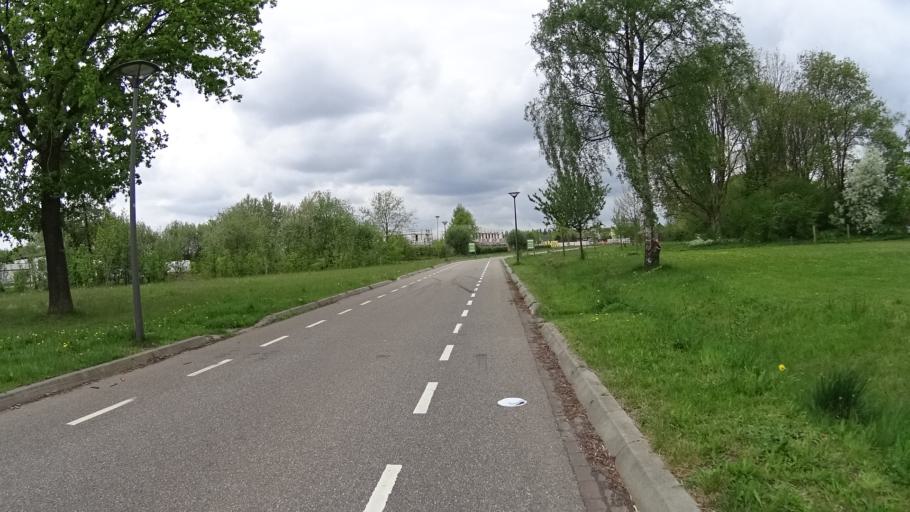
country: NL
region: North Brabant
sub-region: Gemeente Veghel
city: Veghel
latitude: 51.6099
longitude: 5.5593
